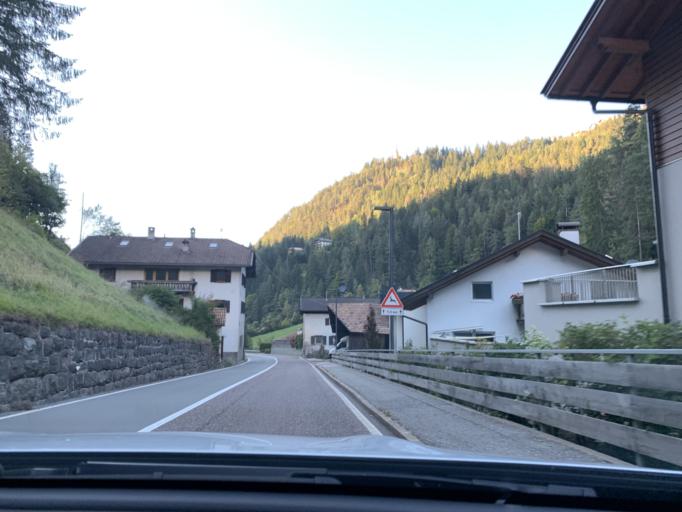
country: IT
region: Trentino-Alto Adige
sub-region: Bolzano
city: Nova Ponente
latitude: 46.4307
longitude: 11.4771
